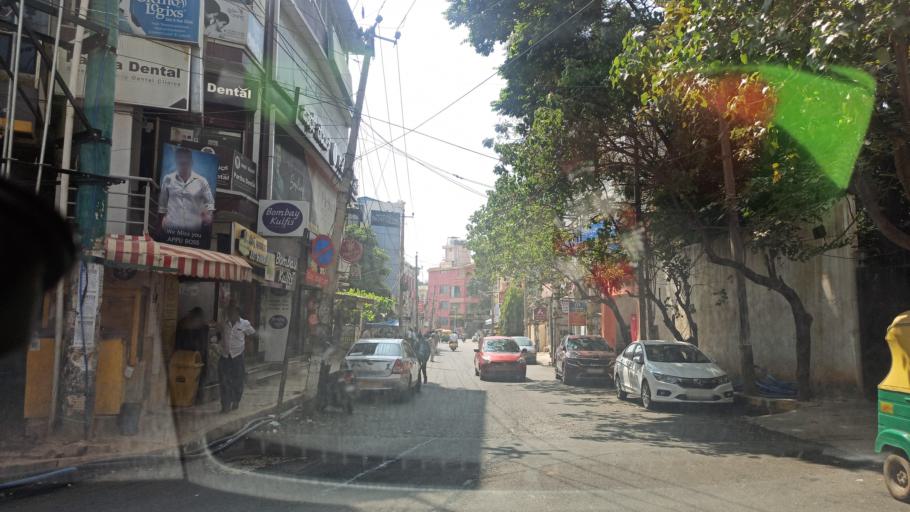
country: IN
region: Karnataka
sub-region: Bangalore Urban
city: Yelahanka
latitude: 13.0506
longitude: 77.5976
